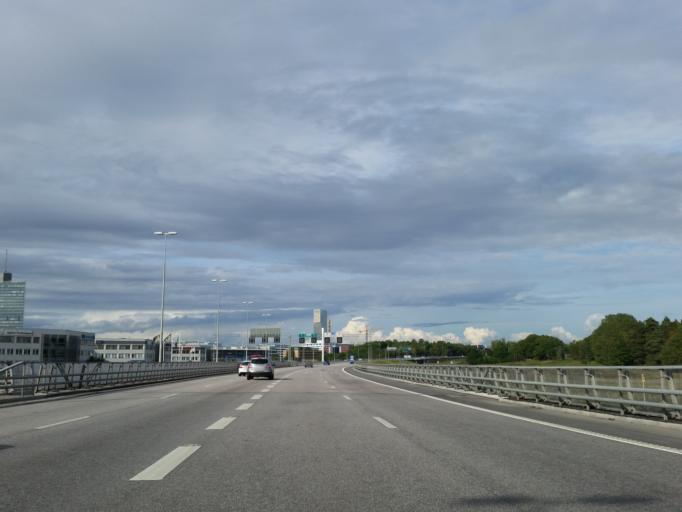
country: SE
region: Stockholm
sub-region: Stockholms Kommun
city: Kista
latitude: 59.3925
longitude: 17.9488
